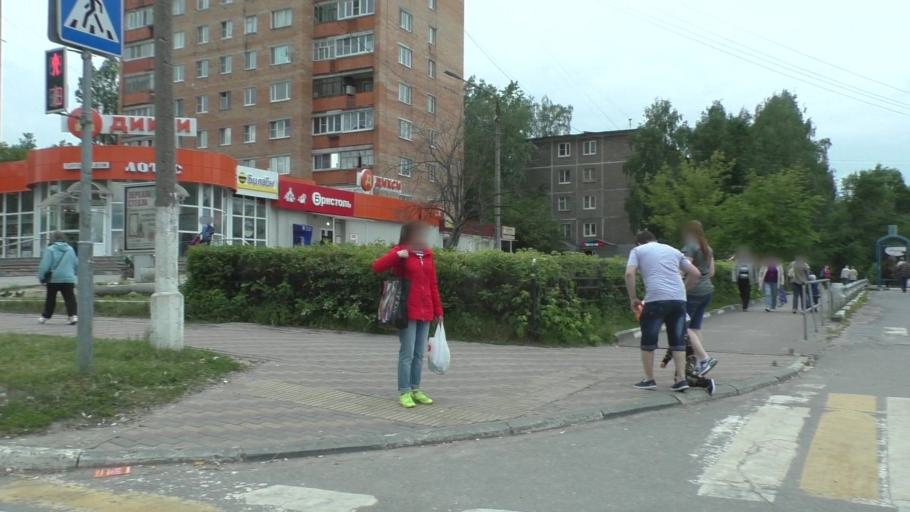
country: RU
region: Moskovskaya
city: Yegor'yevsk
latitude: 55.3688
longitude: 39.0663
